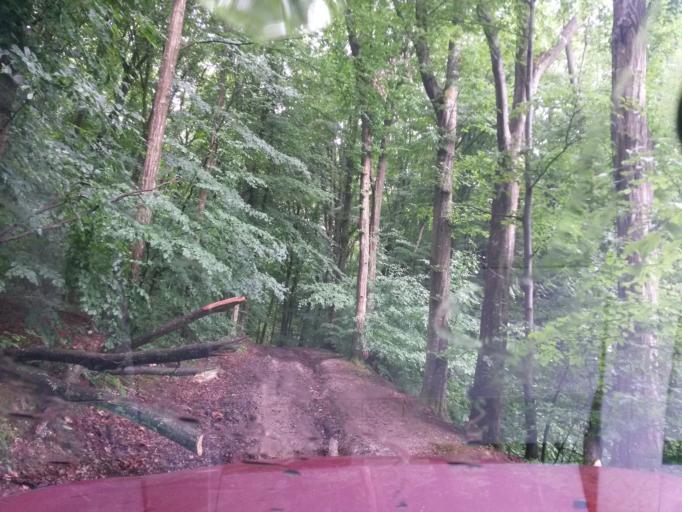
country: SK
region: Kosicky
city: Kosice
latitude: 48.7206
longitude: 21.1677
